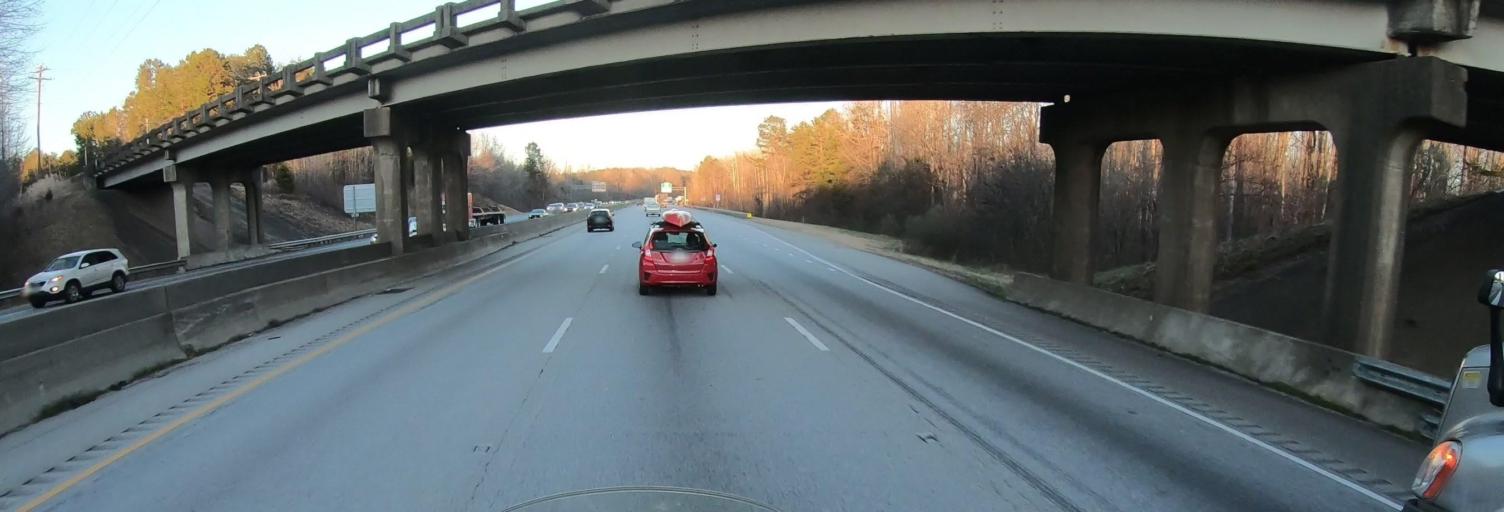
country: US
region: North Carolina
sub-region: Gaston County
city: Bessemer City
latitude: 35.2539
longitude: -81.2893
